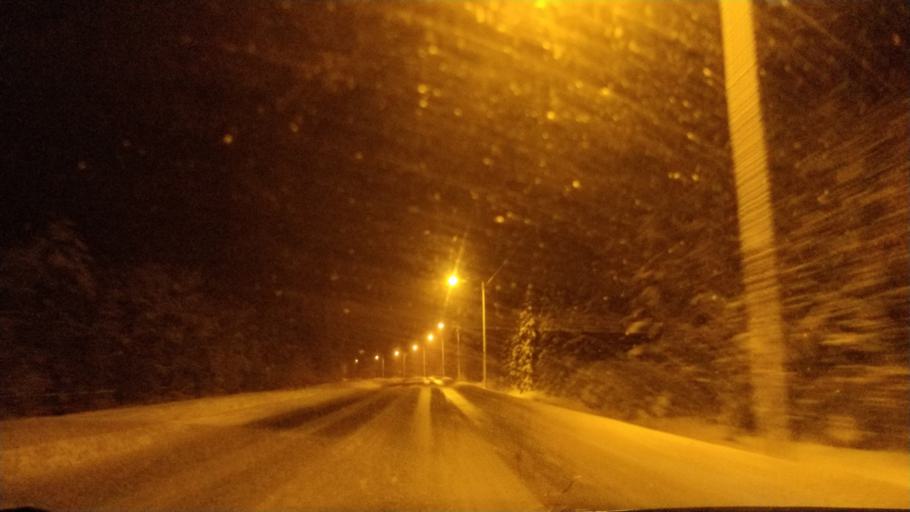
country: FI
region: Lapland
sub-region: Rovaniemi
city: Rovaniemi
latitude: 66.4055
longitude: 25.3943
